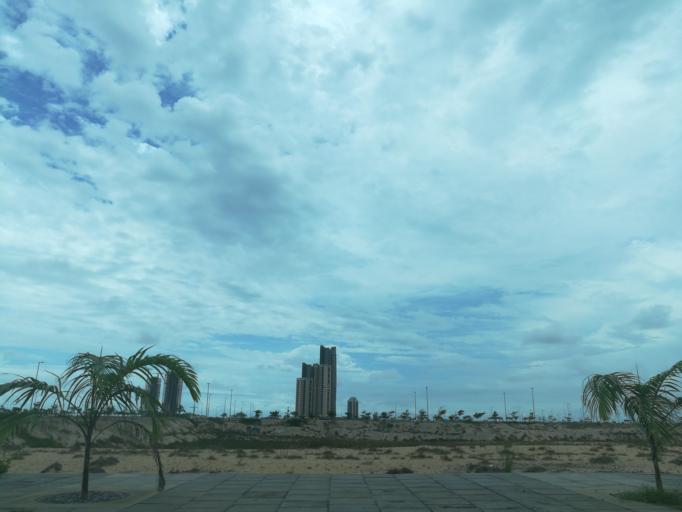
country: NG
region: Lagos
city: Ikoyi
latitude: 6.4127
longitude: 3.4187
